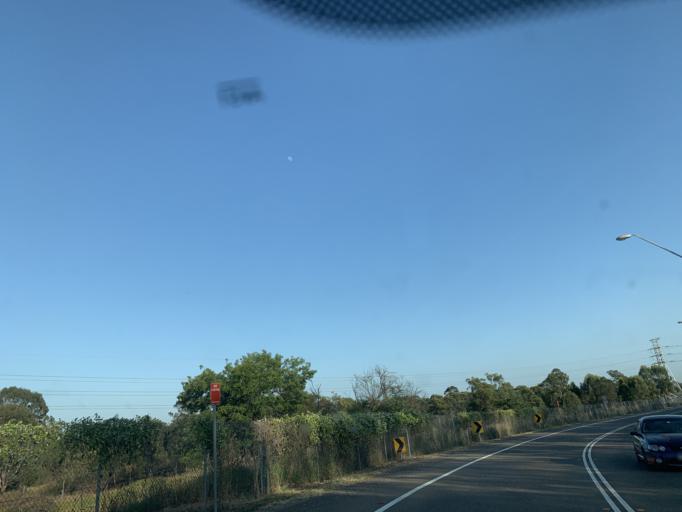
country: AU
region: New South Wales
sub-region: Fairfield
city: Horsley Park
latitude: -33.8083
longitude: 150.8641
